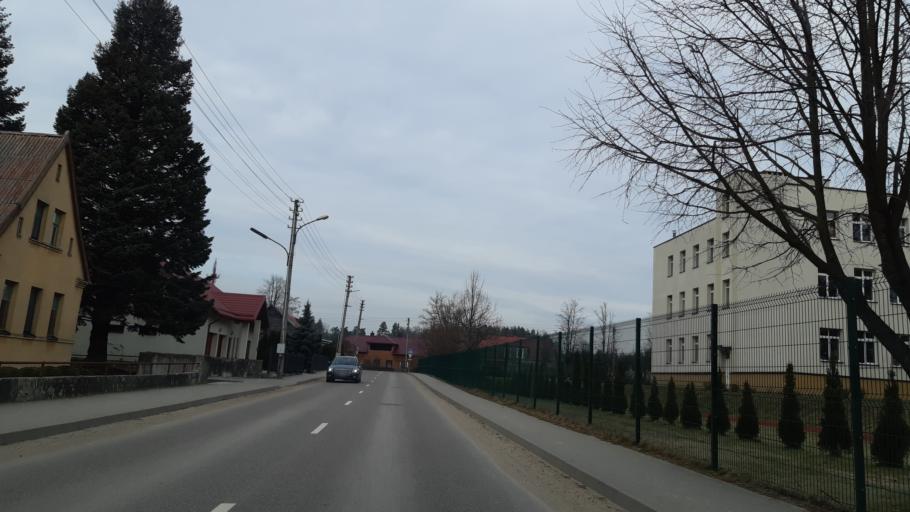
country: LT
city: Kazlu Ruda
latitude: 54.7530
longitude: 23.4957
